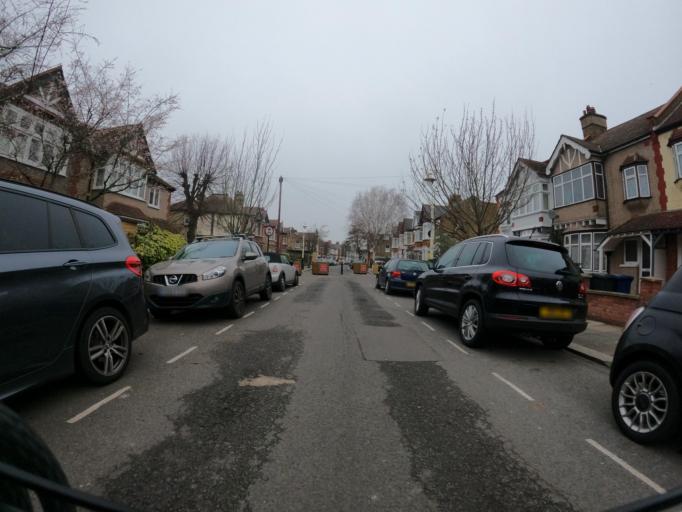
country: GB
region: England
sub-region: Greater London
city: Brentford
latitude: 51.5036
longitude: -0.3246
